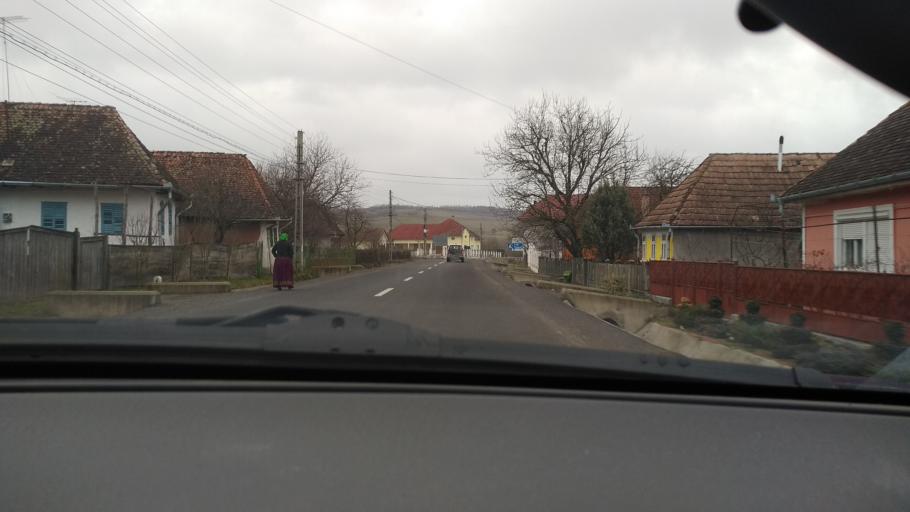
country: RO
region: Mures
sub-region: Comuna Magherani
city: Magherani
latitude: 46.5592
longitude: 24.8956
